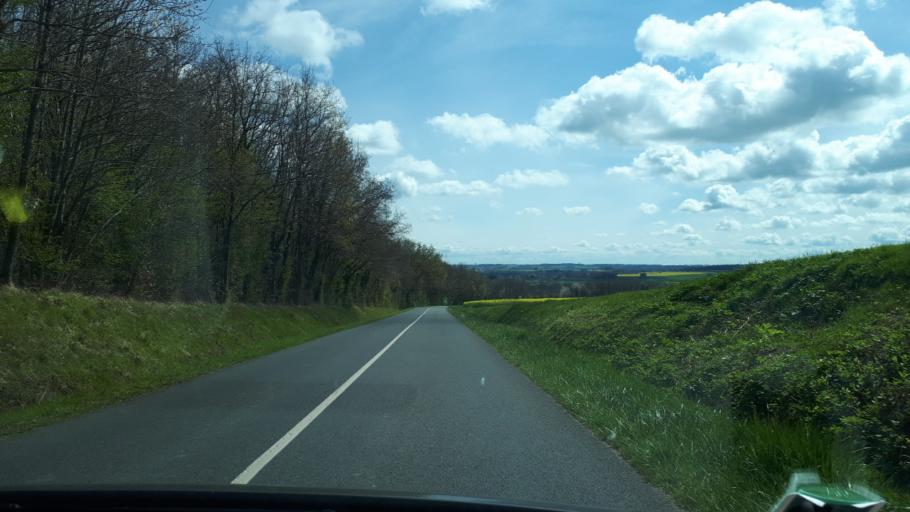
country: FR
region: Centre
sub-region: Departement du Loir-et-Cher
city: Lunay
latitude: 47.8162
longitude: 0.9460
